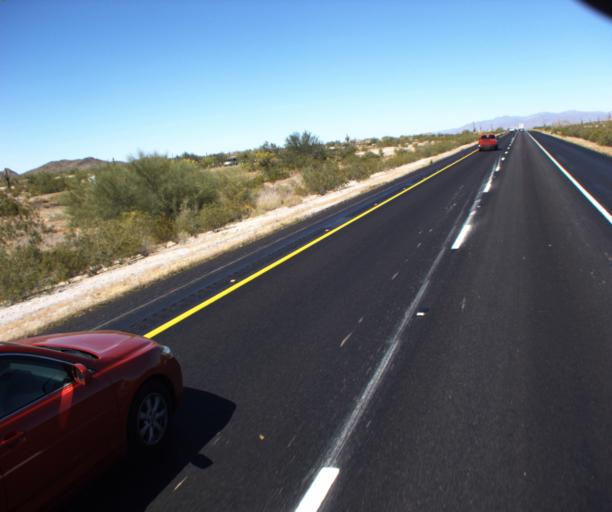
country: US
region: Arizona
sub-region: Maricopa County
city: Buckeye
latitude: 33.2608
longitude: -112.6348
